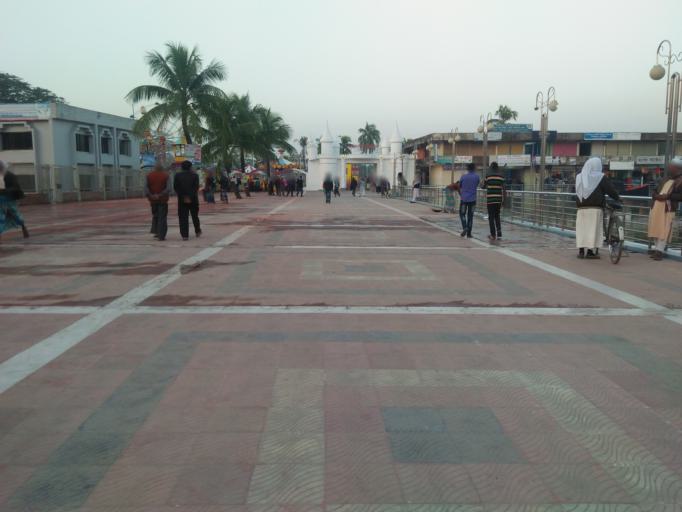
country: BD
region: Khulna
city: Uttar Char Fasson
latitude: 22.1866
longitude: 90.7594
